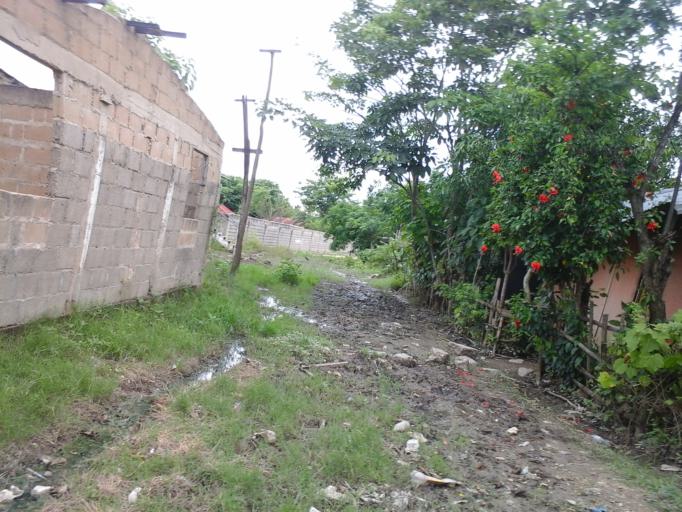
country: CO
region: Bolivar
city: San Pablo
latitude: 10.1441
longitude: -75.2750
